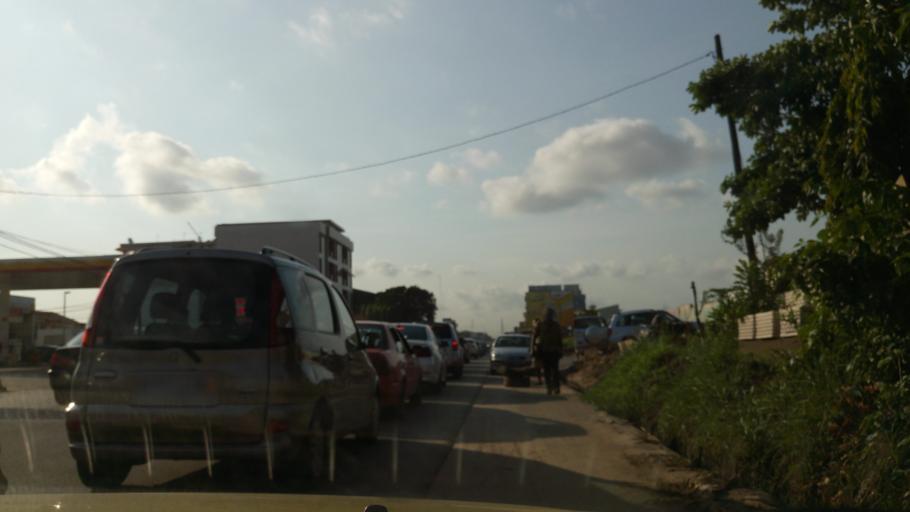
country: CI
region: Lagunes
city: Abobo
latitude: 5.3889
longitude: -3.9750
